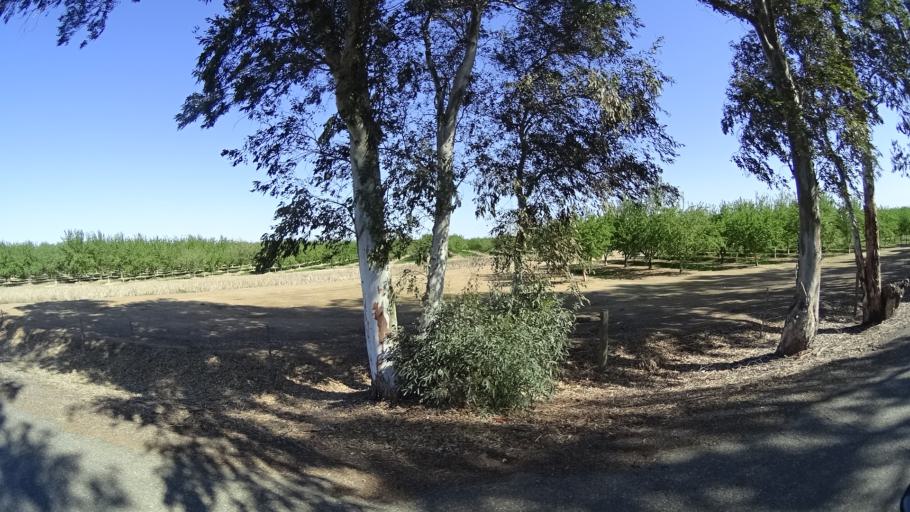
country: US
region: California
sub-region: Glenn County
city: Hamilton City
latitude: 39.7824
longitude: -122.0742
